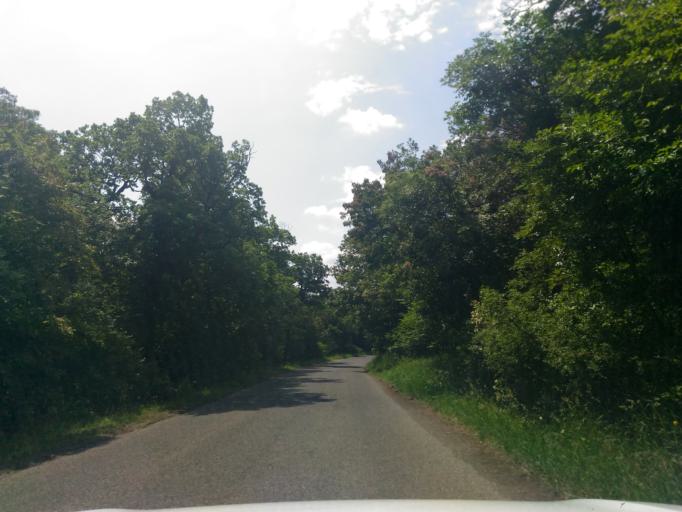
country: HU
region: Baranya
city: Pecs
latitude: 46.0967
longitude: 18.2275
